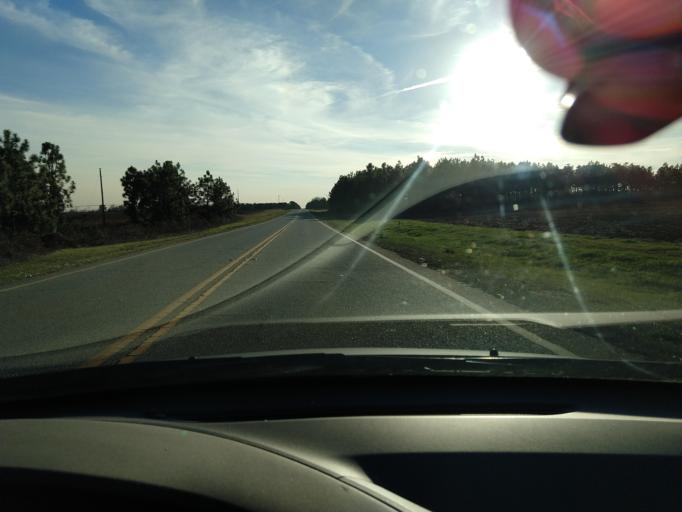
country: US
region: Georgia
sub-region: Sumter County
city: Americus
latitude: 32.1380
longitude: -84.1447
